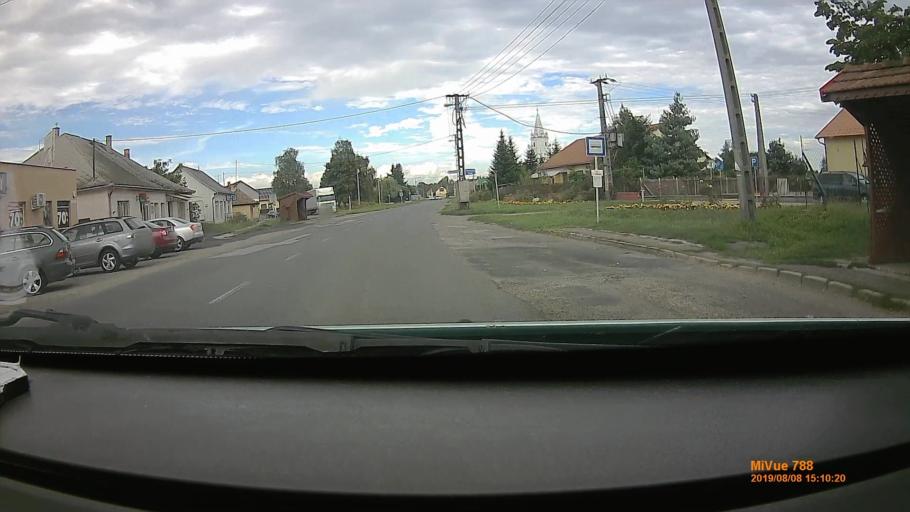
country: HU
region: Szabolcs-Szatmar-Bereg
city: Tunyogmatolcs
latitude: 47.9702
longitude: 22.4524
